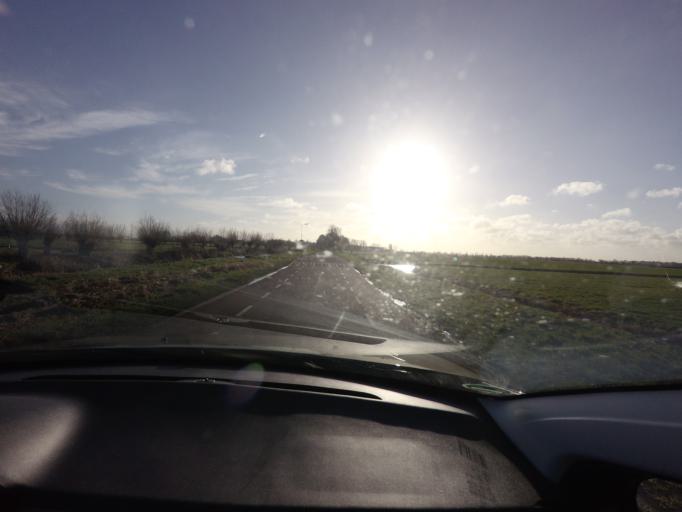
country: NL
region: Utrecht
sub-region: Stichtse Vecht
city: Breukelen
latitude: 52.1902
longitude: 4.9701
